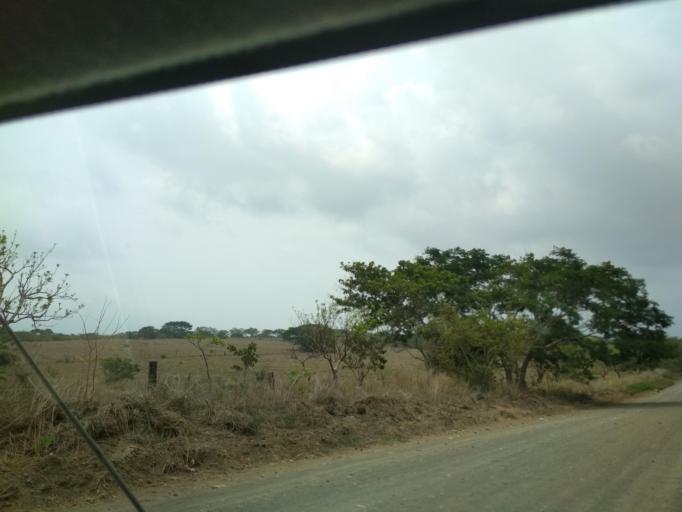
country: MX
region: Veracruz
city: Paso del Toro
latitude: 19.0136
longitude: -96.1340
